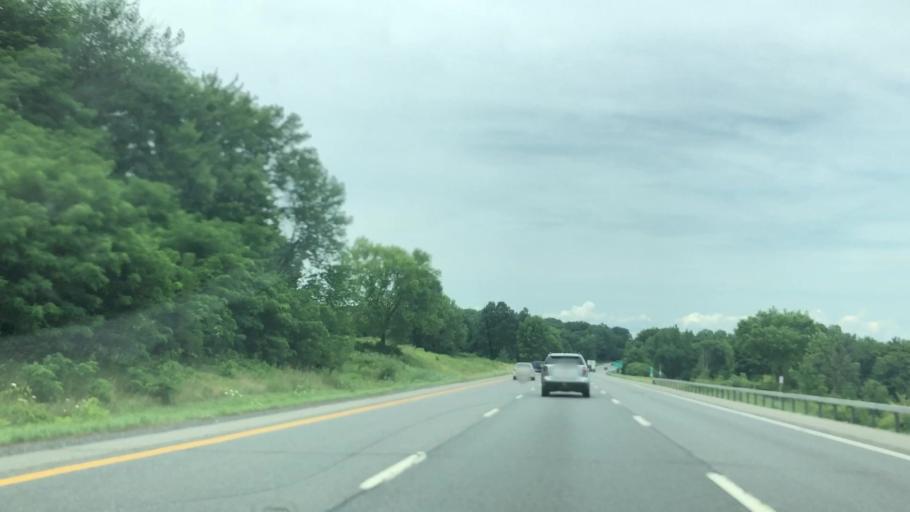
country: US
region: New York
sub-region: Saratoga County
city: Country Knolls
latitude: 42.9157
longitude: -73.7963
